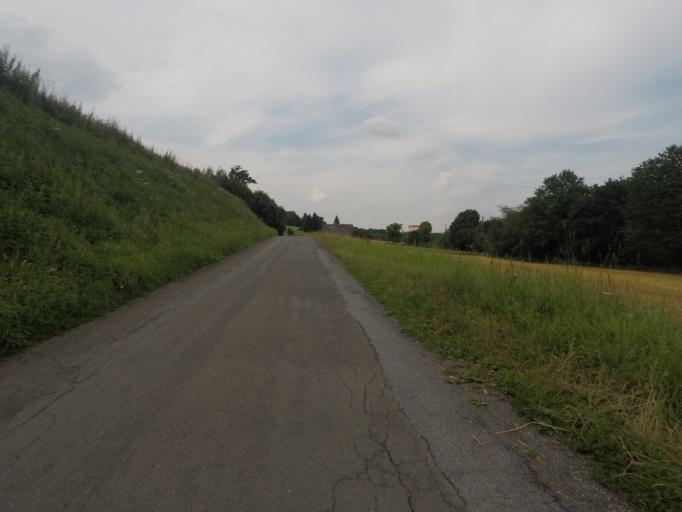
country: DE
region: North Rhine-Westphalia
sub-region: Regierungsbezirk Detmold
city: Herford
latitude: 52.0917
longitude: 8.6242
